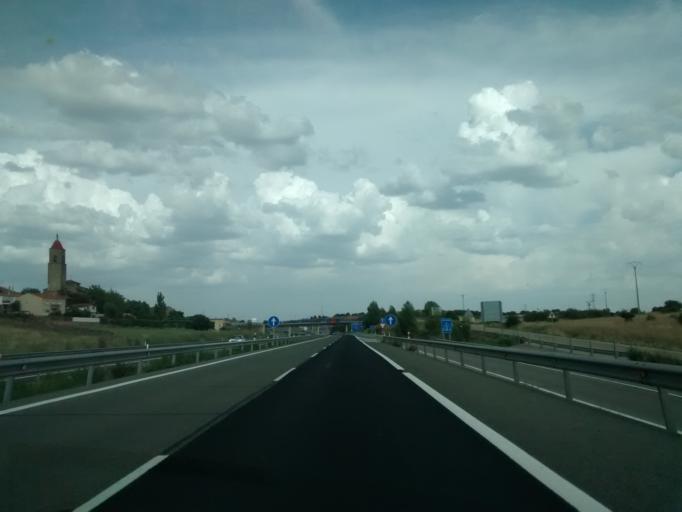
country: ES
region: Castille-La Mancha
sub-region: Provincia de Guadalajara
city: Alcolea del Pinar
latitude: 41.0346
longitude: -2.4710
